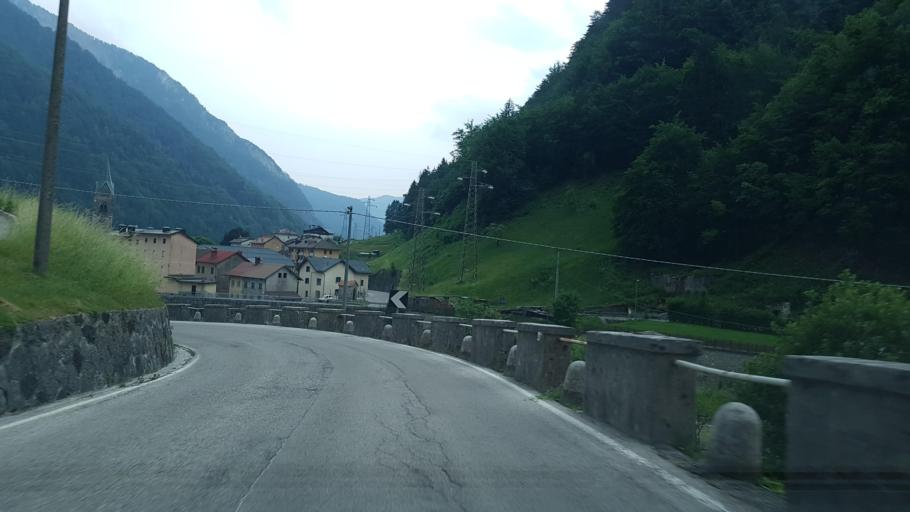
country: IT
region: Friuli Venezia Giulia
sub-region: Provincia di Udine
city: Pontebba
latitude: 46.5093
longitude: 13.3018
